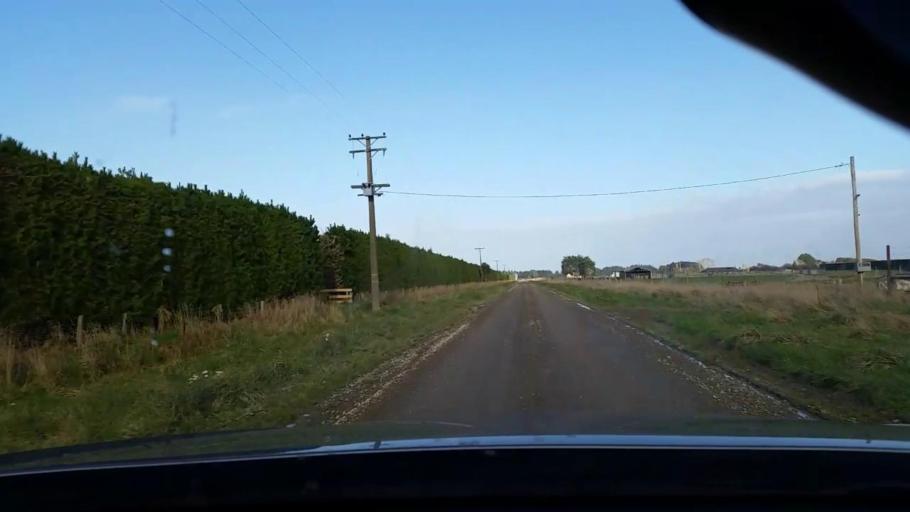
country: NZ
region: Southland
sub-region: Invercargill City
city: Invercargill
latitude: -46.2840
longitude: 168.2947
